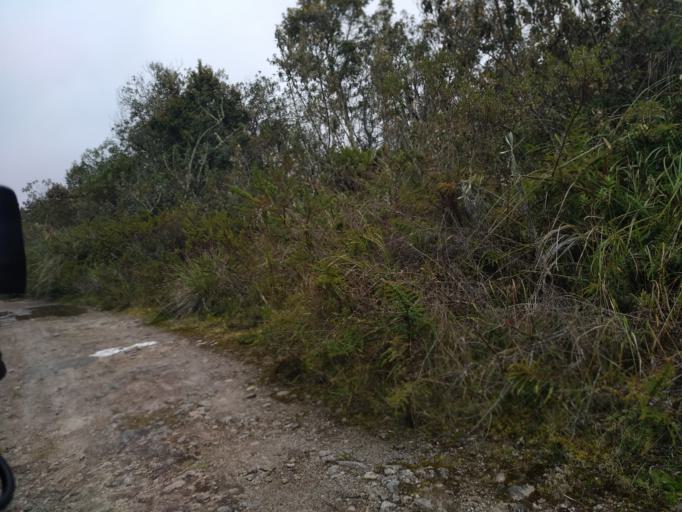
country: EC
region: Carchi
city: San Gabriel
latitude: 0.7016
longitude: -77.8424
